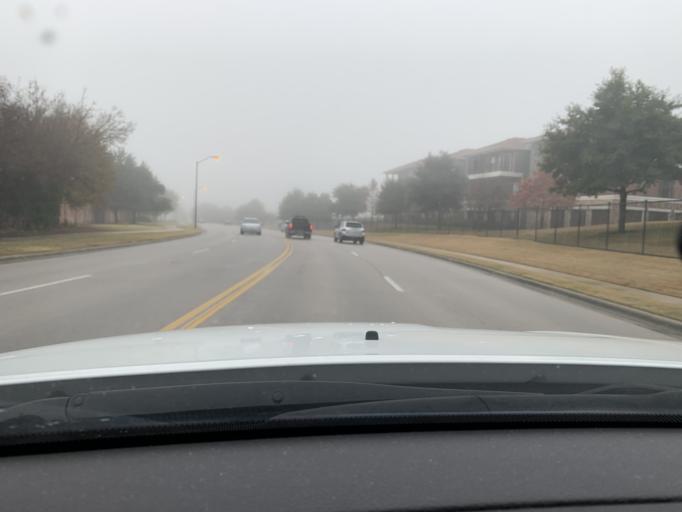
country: US
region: Texas
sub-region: Williamson County
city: Round Rock
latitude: 30.5672
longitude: -97.6834
